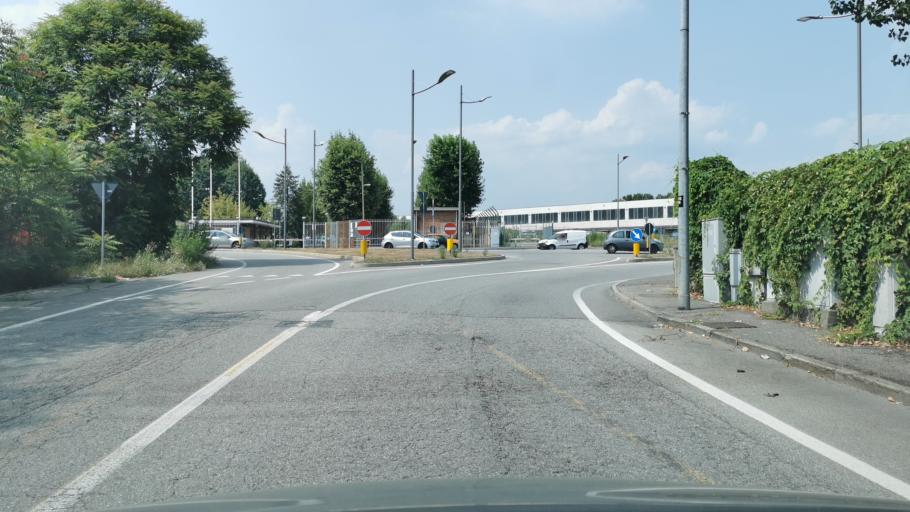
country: IT
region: Piedmont
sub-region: Provincia di Torino
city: Settimo Torinese
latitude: 45.1239
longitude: 7.7295
